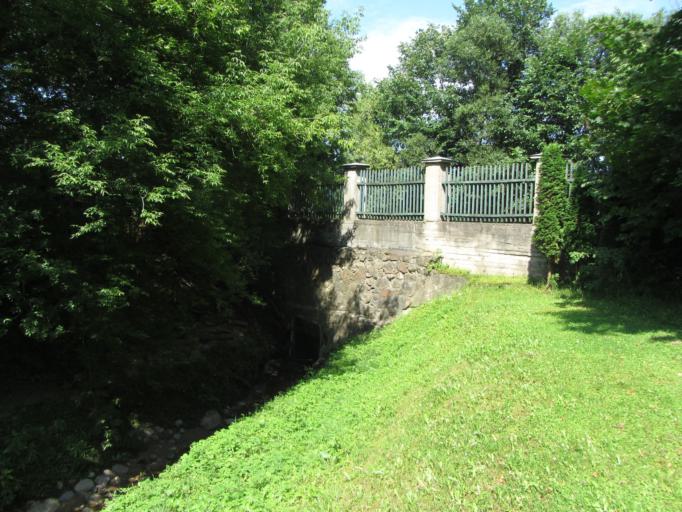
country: LT
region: Vilnius County
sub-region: Vilnius
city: Vilnius
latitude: 54.7303
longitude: 25.2919
